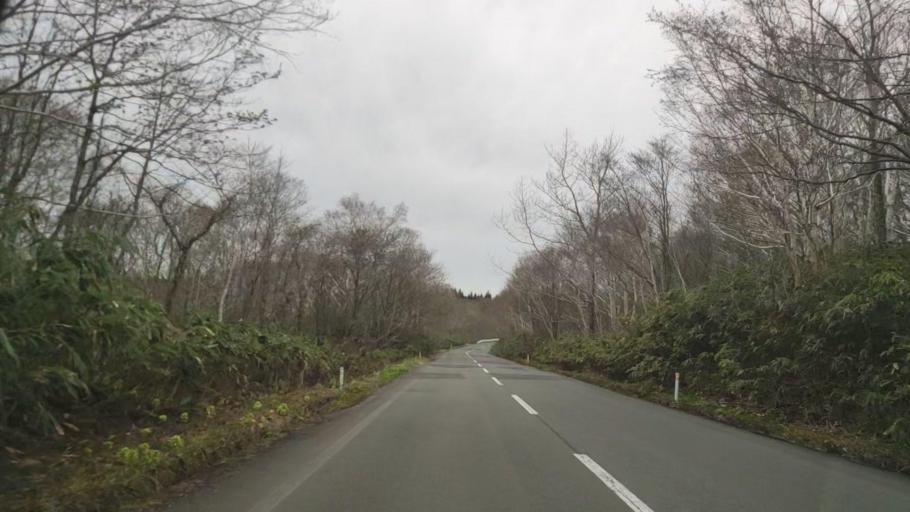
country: JP
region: Akita
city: Hanawa
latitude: 40.4079
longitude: 140.8512
